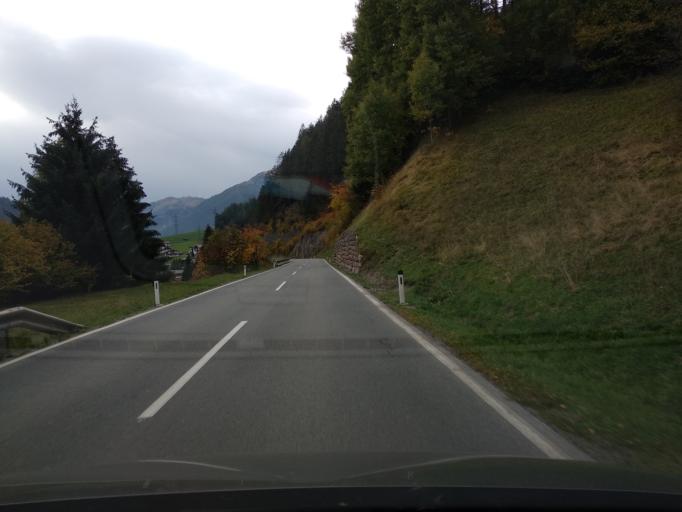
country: AT
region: Tyrol
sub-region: Politischer Bezirk Landeck
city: Flirsch
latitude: 47.1482
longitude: 10.3352
